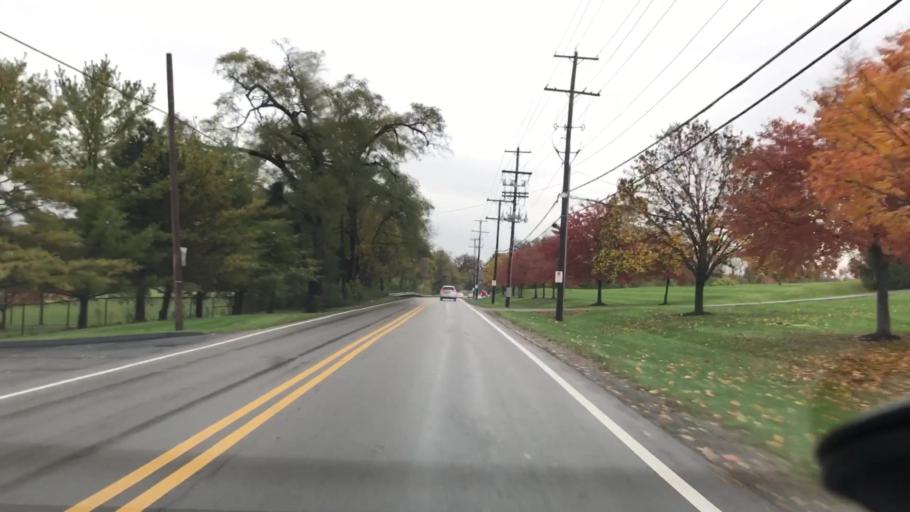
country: US
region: Ohio
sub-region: Franklin County
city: Minerva Park
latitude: 40.0465
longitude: -82.9292
